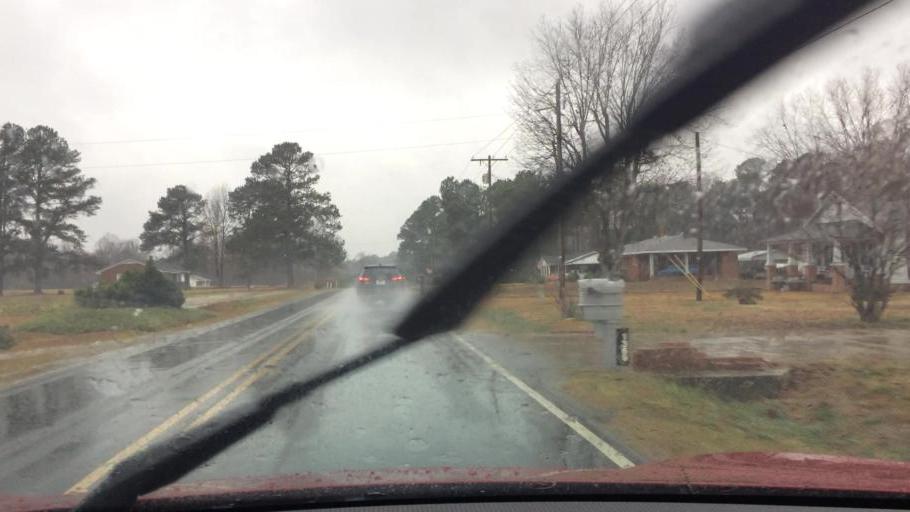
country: US
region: North Carolina
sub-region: Wayne County
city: Goldsboro
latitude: 35.4126
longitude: -77.9295
